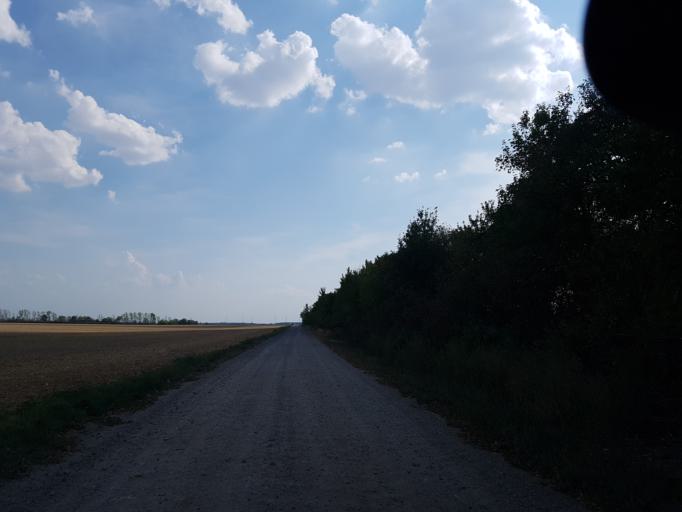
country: DE
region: Brandenburg
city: Treuenbrietzen
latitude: 51.9975
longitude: 12.8691
